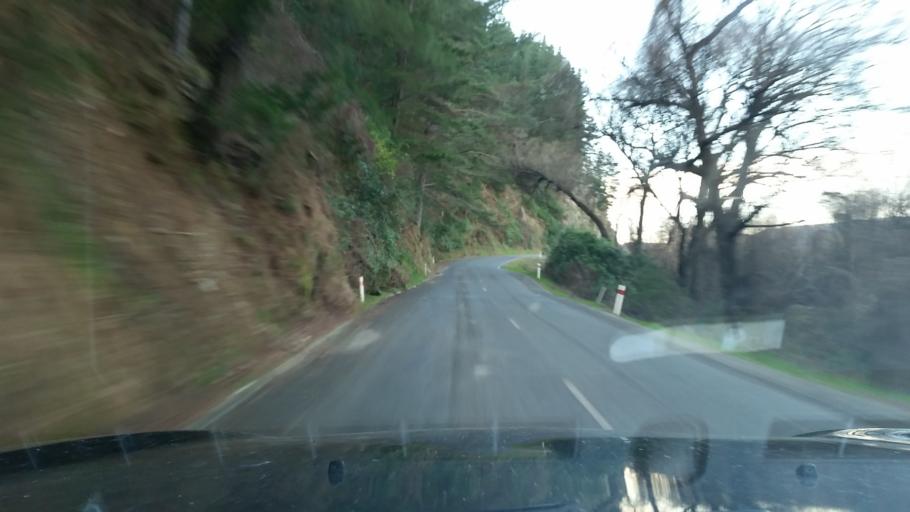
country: NZ
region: Marlborough
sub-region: Marlborough District
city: Blenheim
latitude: -41.5195
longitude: 173.6141
